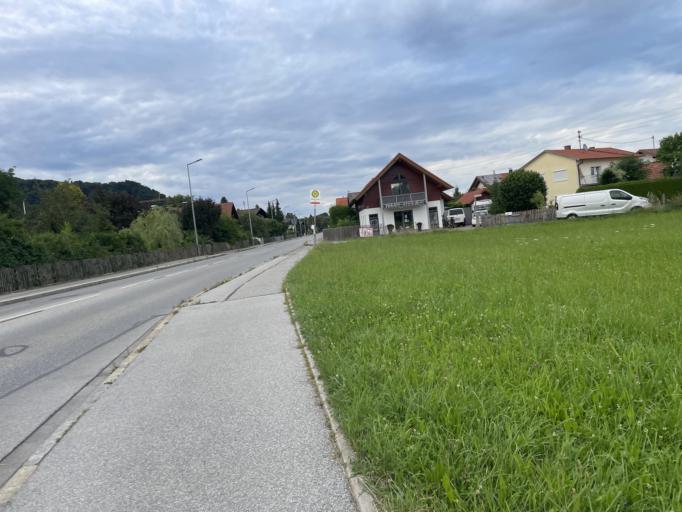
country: DE
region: Bavaria
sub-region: Upper Bavaria
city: Peissenberg
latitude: 47.7839
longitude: 11.0554
